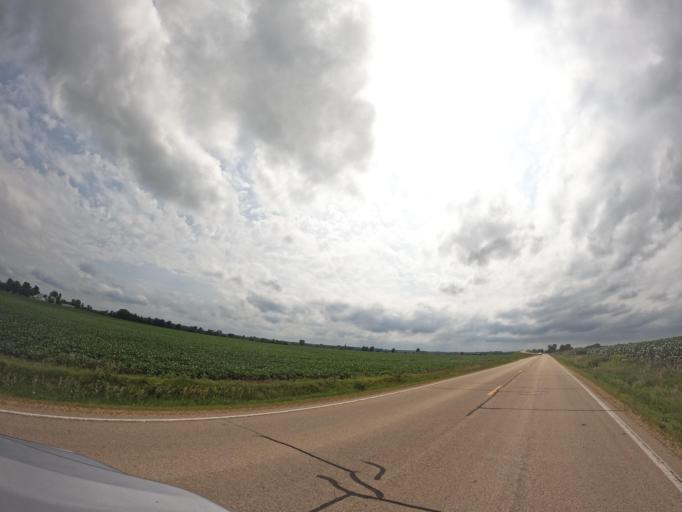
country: US
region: Iowa
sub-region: Clinton County
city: De Witt
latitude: 41.7859
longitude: -90.5597
